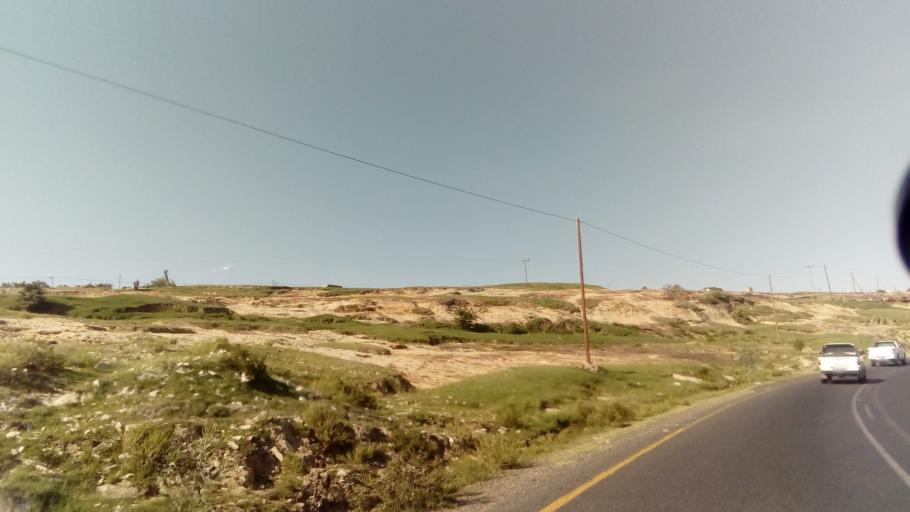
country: LS
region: Berea
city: Teyateyaneng
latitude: -29.1471
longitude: 27.6967
